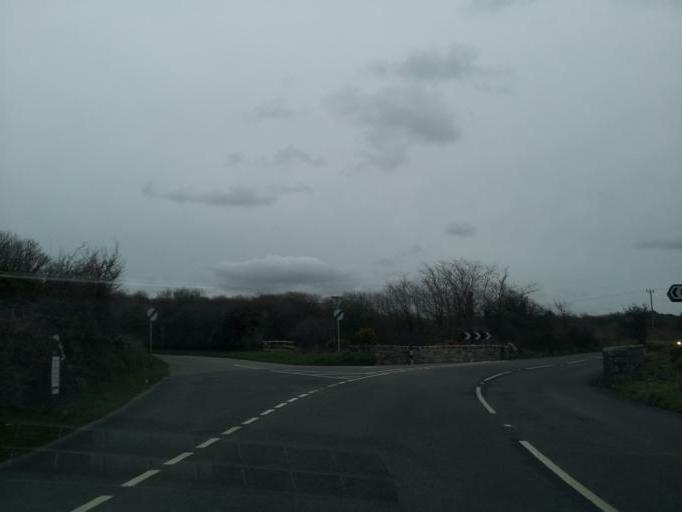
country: GB
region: England
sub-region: Cornwall
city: Redruth
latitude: 50.2601
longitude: -5.2497
